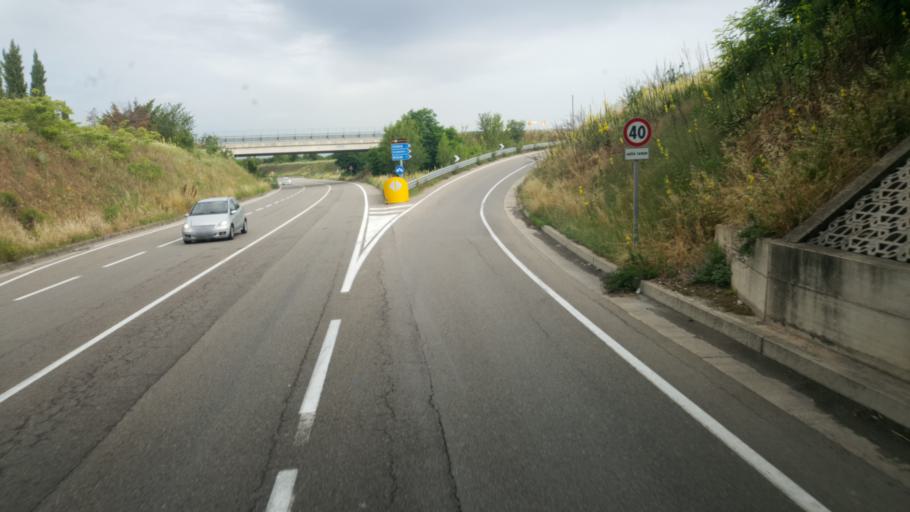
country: IT
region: Emilia-Romagna
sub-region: Provincia di Modena
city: Vignola
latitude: 44.5066
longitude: 11.0234
